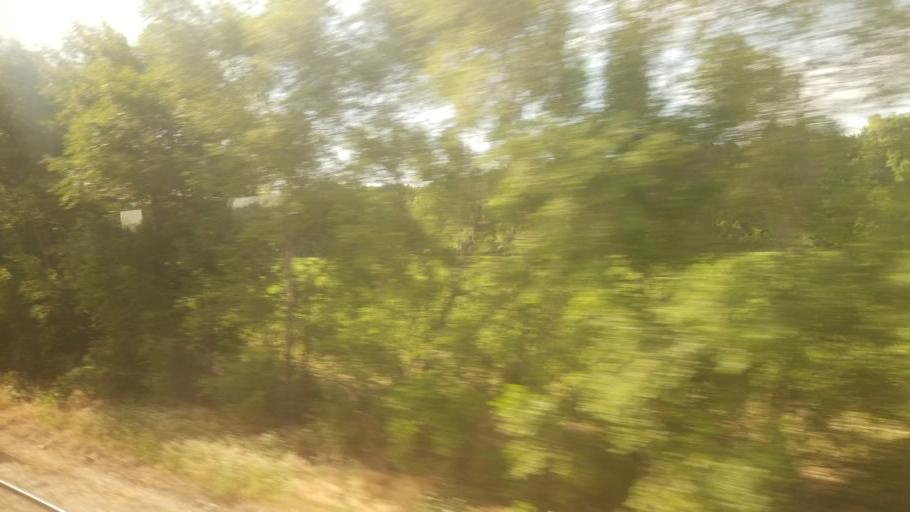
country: US
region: Kansas
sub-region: Johnson County
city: De Soto
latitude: 38.9810
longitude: -94.9454
